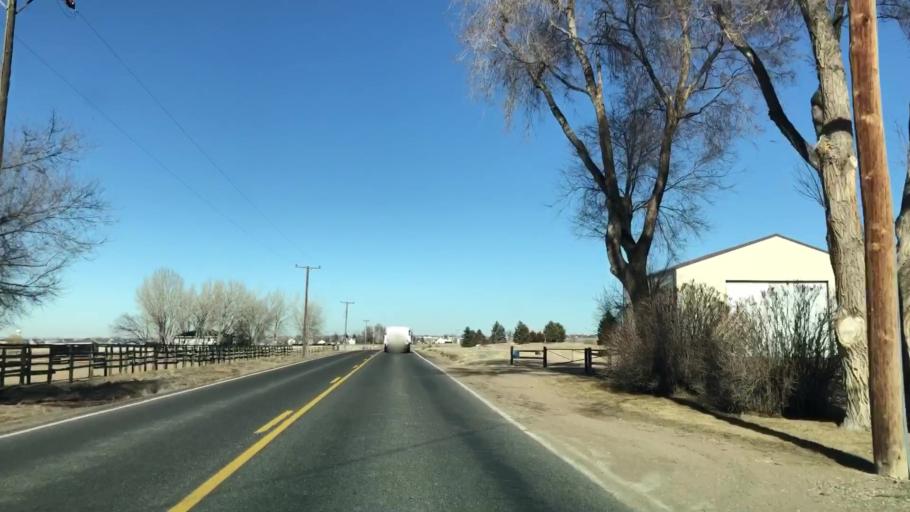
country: US
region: Colorado
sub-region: Weld County
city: Windsor
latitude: 40.4982
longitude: -104.9441
